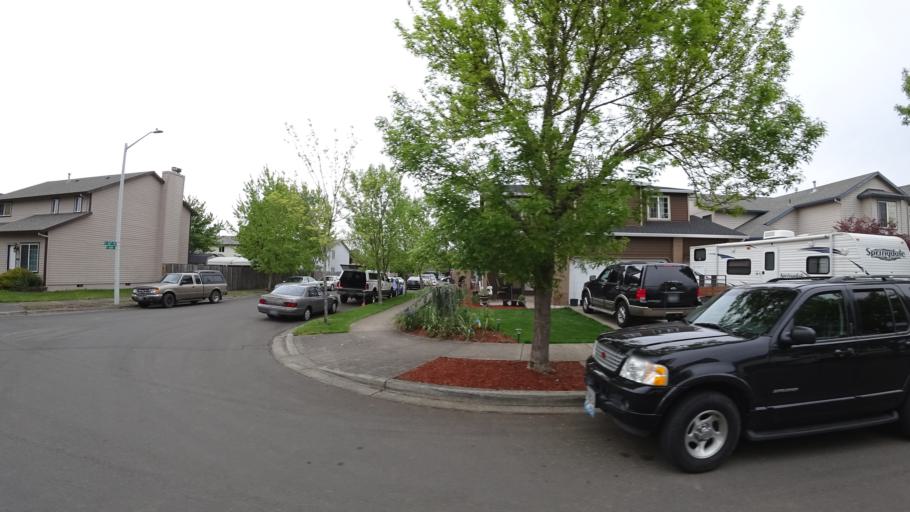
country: US
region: Oregon
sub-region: Washington County
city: Aloha
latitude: 45.5115
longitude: -122.9123
